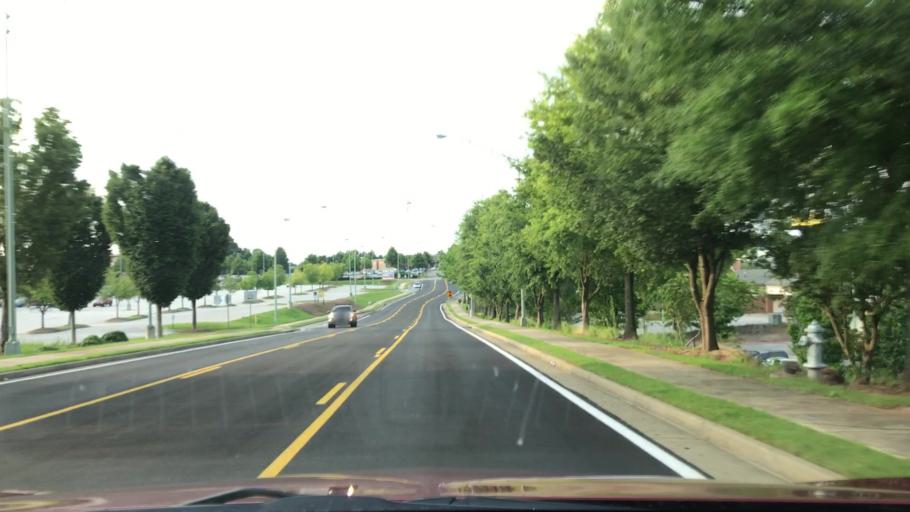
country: US
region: Georgia
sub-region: Gwinnett County
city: Buford
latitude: 34.0723
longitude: -83.9856
